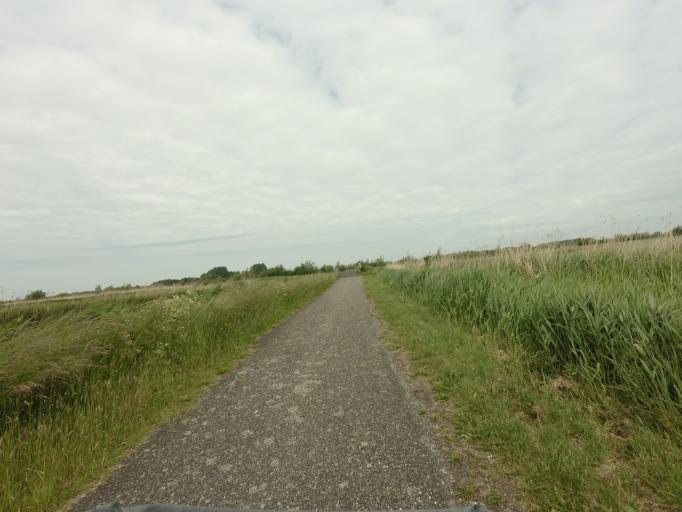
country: NL
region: North Holland
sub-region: Gemeente Medemblik
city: Medemblik
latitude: 52.7401
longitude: 5.1265
